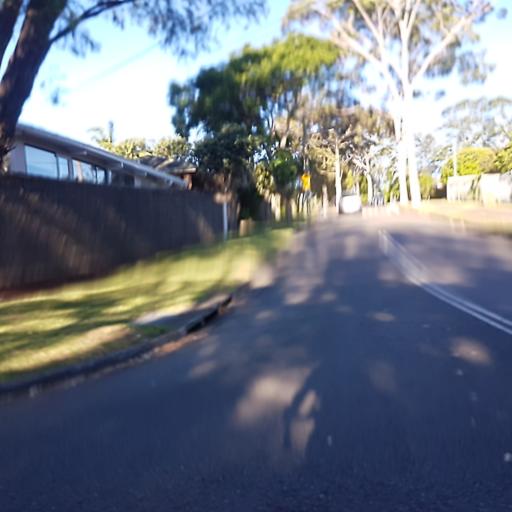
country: AU
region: New South Wales
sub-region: Warringah
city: Forestville
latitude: -33.7559
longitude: 151.2146
